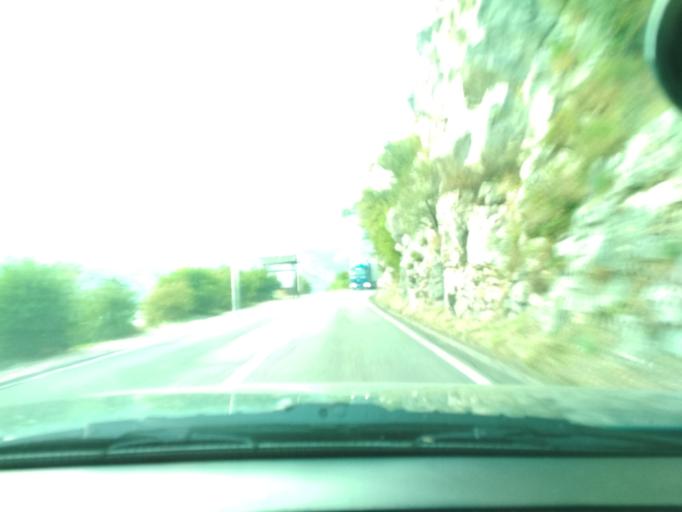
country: ME
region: Kotor
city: Risan
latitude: 42.4918
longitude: 18.6918
